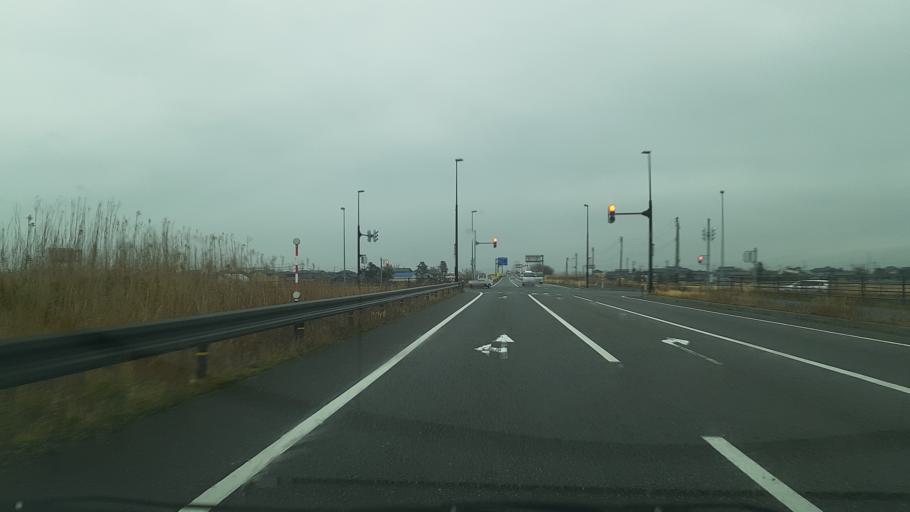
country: JP
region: Niigata
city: Kameda-honcho
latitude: 37.8739
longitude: 139.1548
